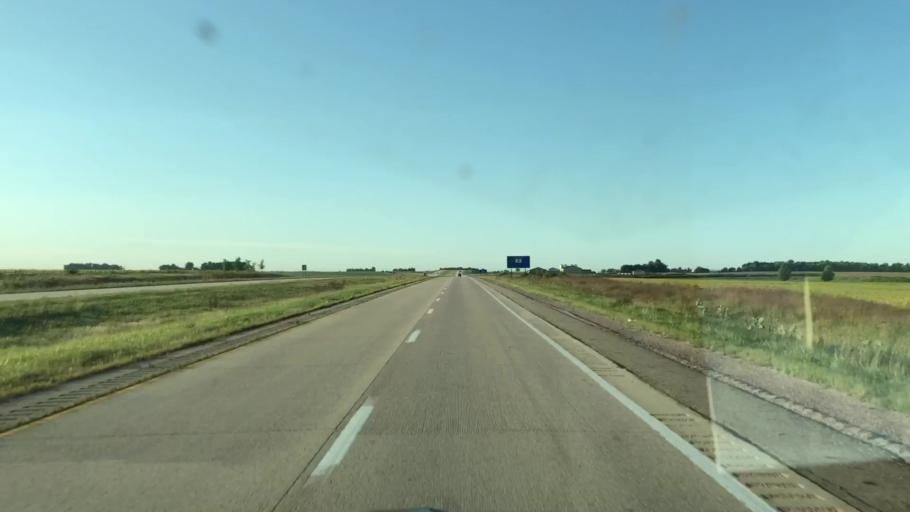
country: US
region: Iowa
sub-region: Osceola County
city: Sibley
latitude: 43.4462
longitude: -95.7136
